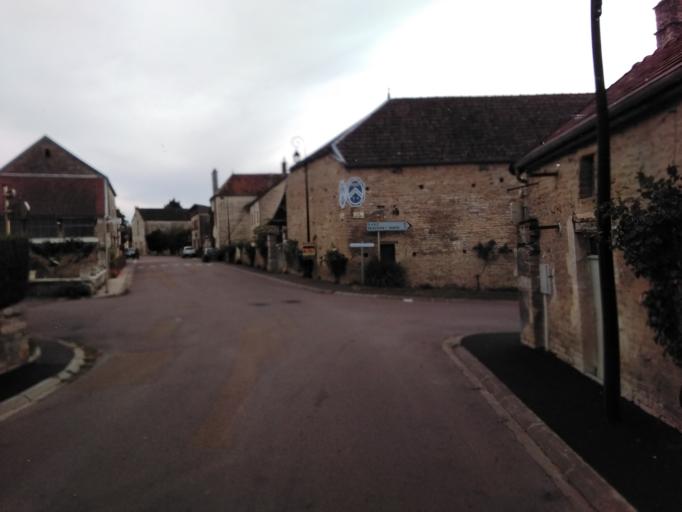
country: FR
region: Champagne-Ardenne
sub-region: Departement de l'Aube
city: Les Riceys
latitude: 47.9381
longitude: 4.3534
